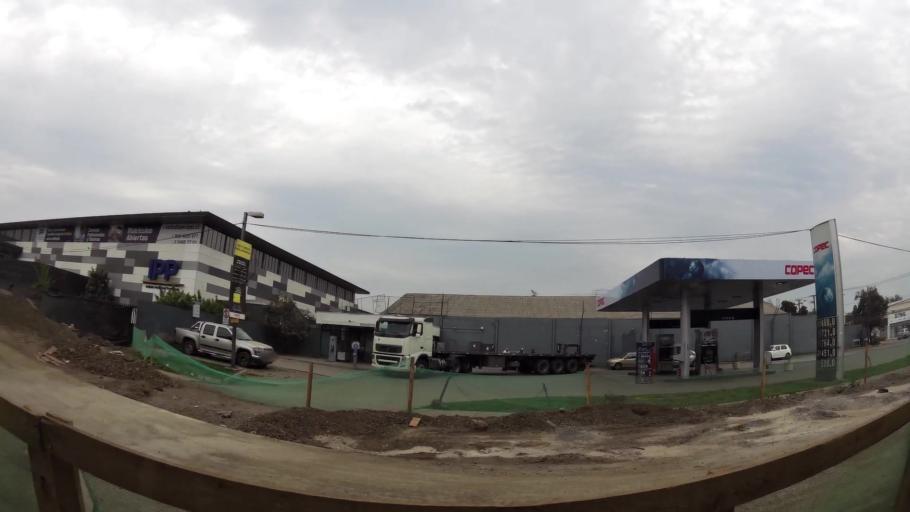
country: CL
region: Santiago Metropolitan
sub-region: Provincia de Santiago
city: Santiago
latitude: -33.4790
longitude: -70.6218
